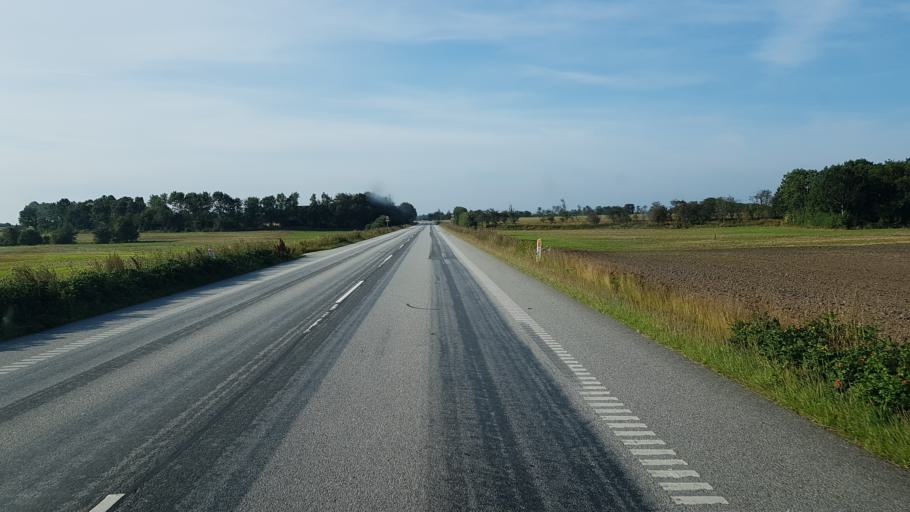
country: DK
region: South Denmark
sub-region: Haderslev Kommune
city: Vojens
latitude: 55.2875
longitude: 9.2897
